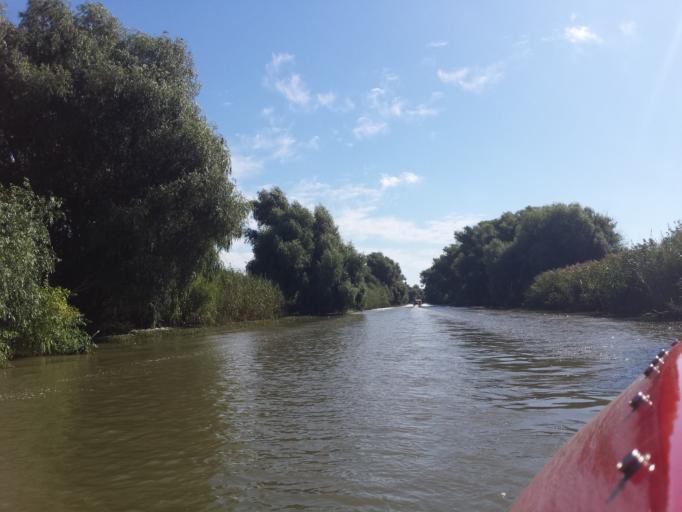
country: RO
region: Tulcea
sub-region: Comuna Mahmudia
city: Mahmudia
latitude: 45.2387
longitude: 29.1198
